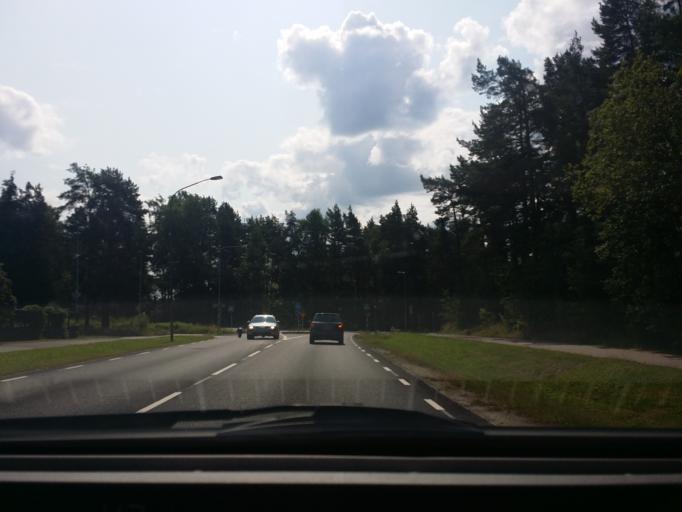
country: SE
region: Vaestmanland
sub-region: Vasteras
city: Vasteras
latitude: 59.6047
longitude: 16.5945
